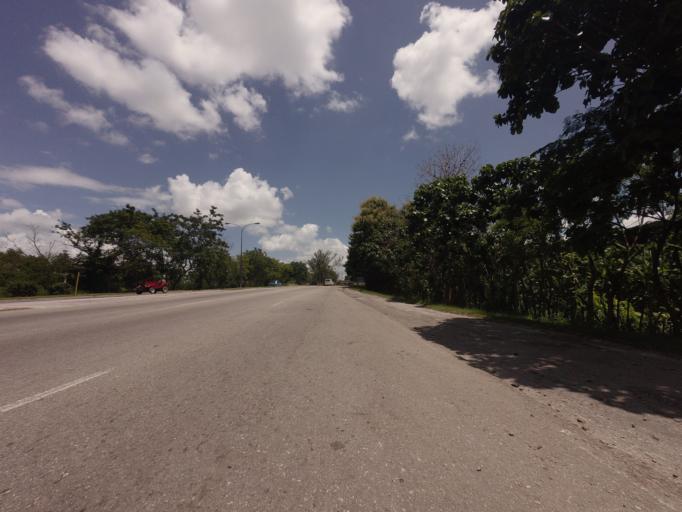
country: CU
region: La Habana
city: Arroyo Naranjo
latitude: 23.0428
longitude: -82.3672
